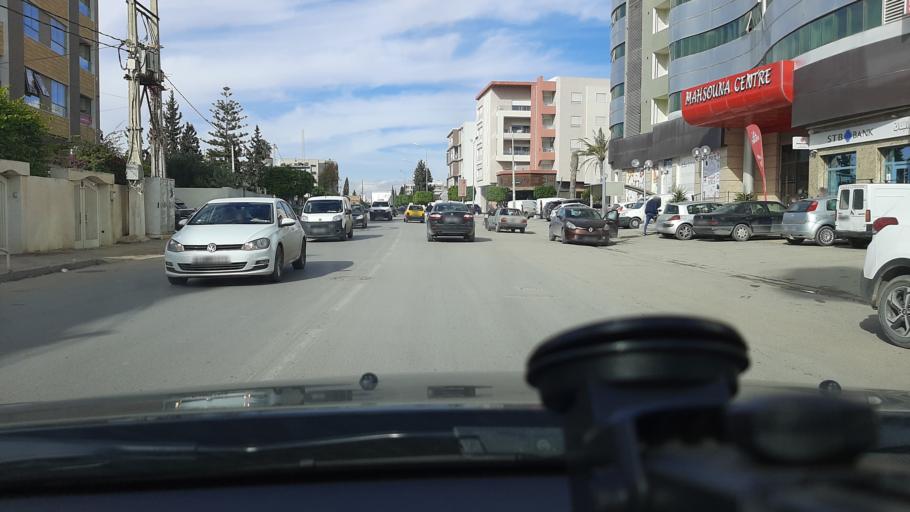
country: TN
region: Safaqis
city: Sfax
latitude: 34.7624
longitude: 10.7286
